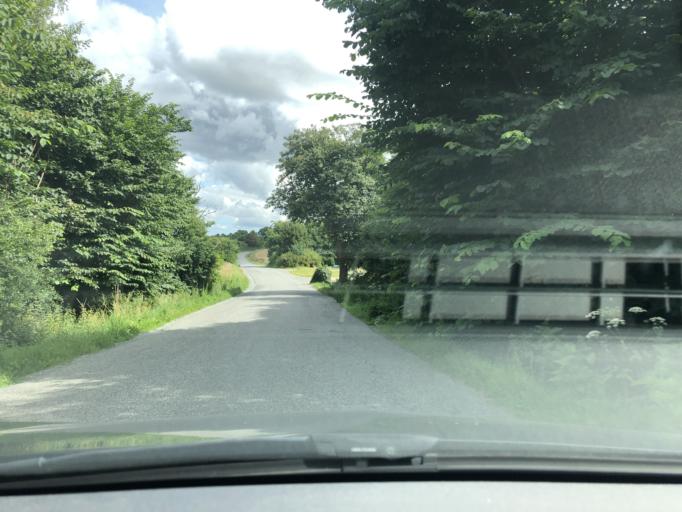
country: DK
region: South Denmark
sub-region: Vejle Kommune
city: Jelling
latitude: 55.6963
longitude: 9.4528
